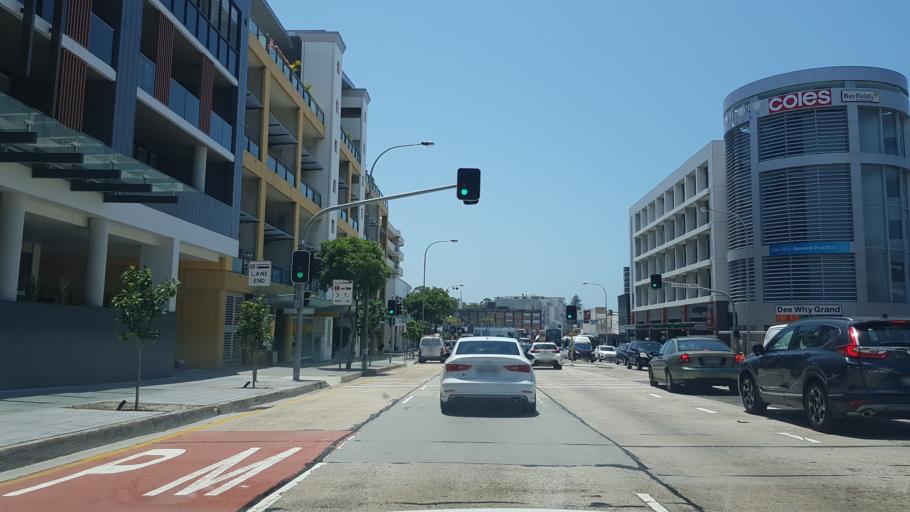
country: AU
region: New South Wales
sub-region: Warringah
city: Narraweena
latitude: -33.7555
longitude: 151.2832
